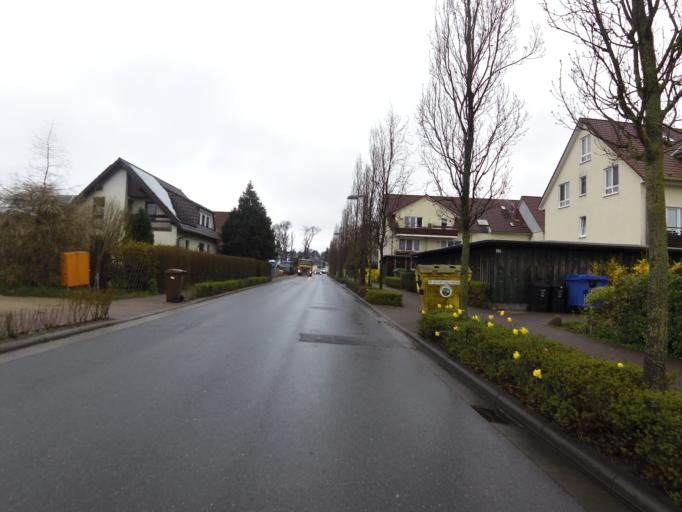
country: DE
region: Mecklenburg-Vorpommern
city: Zingst
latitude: 54.4377
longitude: 12.7015
